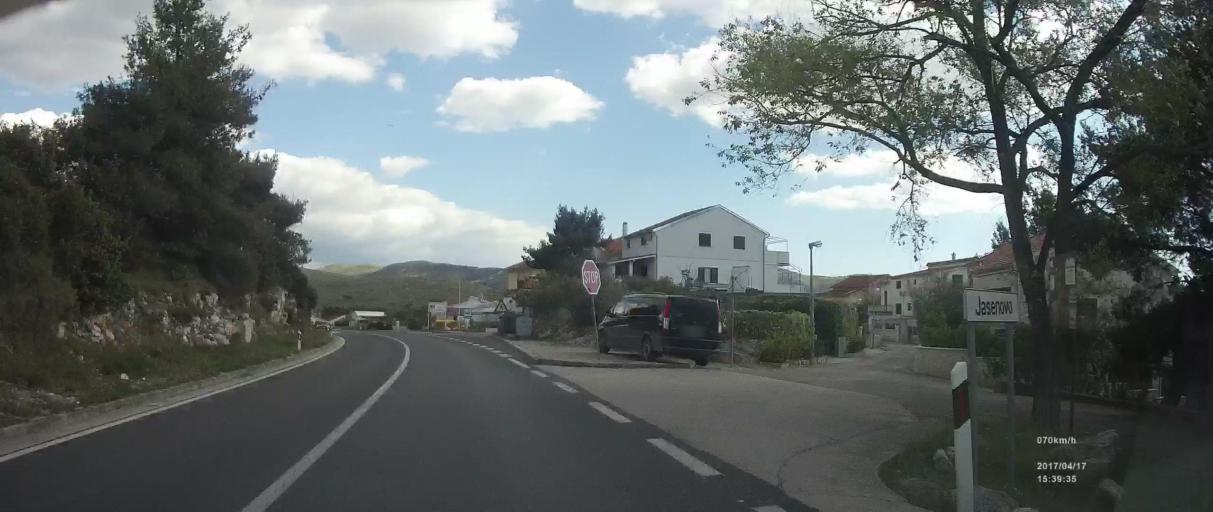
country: HR
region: Sibensko-Kniniska
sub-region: Grad Sibenik
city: Brodarica
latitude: 43.6554
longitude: 15.9469
